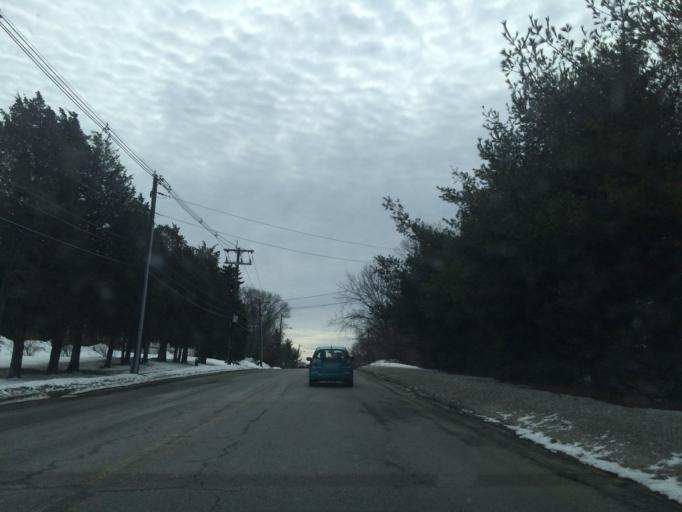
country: US
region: Massachusetts
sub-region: Middlesex County
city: Lexington
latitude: 42.4249
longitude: -71.2313
